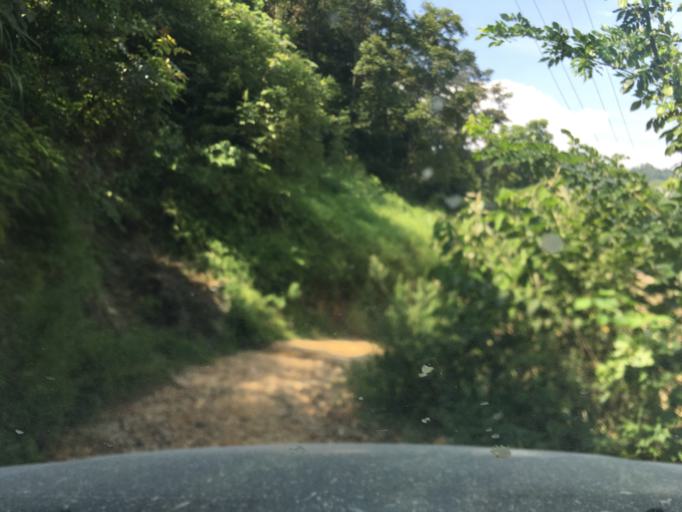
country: CN
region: Guangxi Zhuangzu Zizhiqu
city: Xinzhou
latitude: 25.0438
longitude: 105.8691
